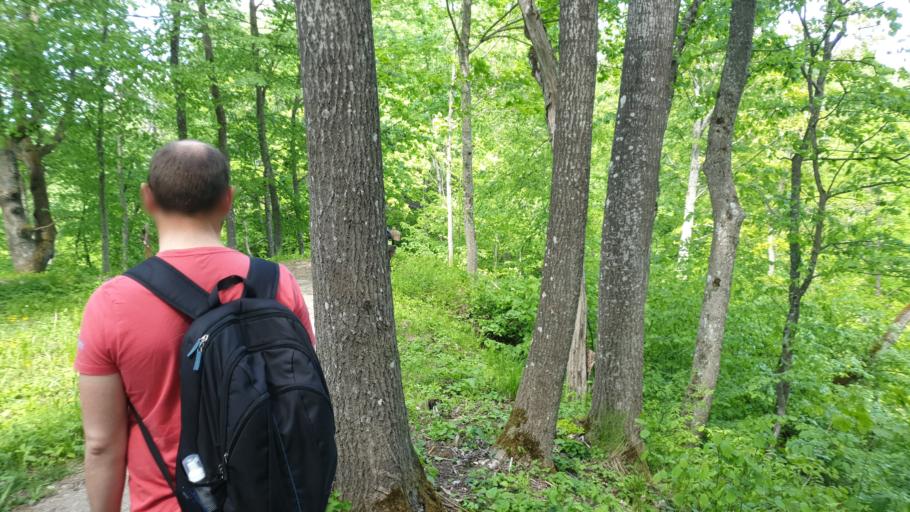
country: LT
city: Moletai
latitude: 55.0727
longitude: 25.4129
